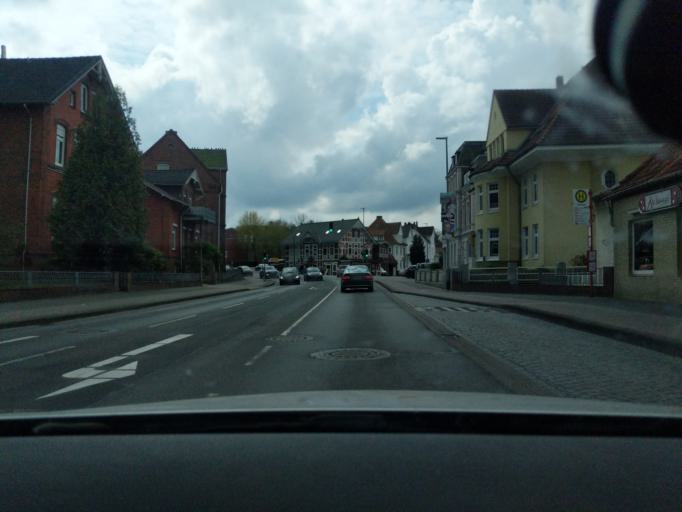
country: DE
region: Lower Saxony
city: Stade
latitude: 53.5934
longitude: 9.4728
